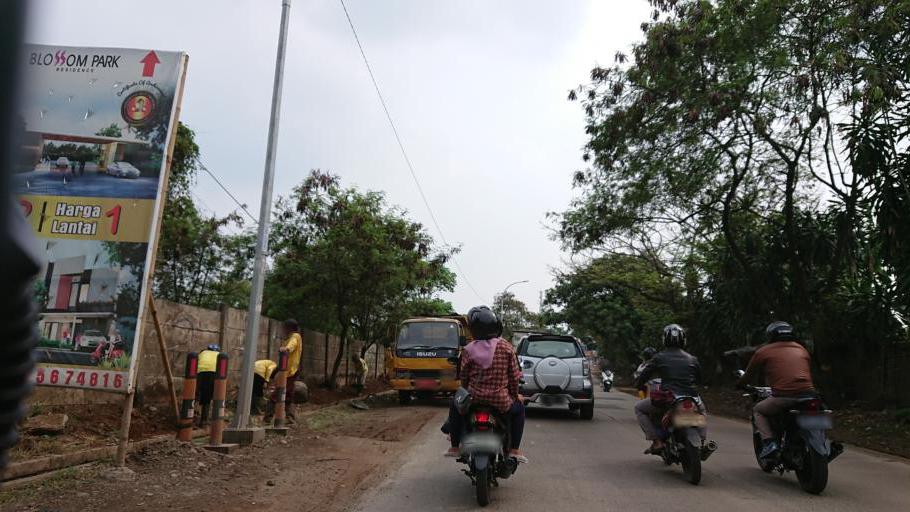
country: ID
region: West Java
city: Serpong
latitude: -6.3782
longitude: 106.6810
